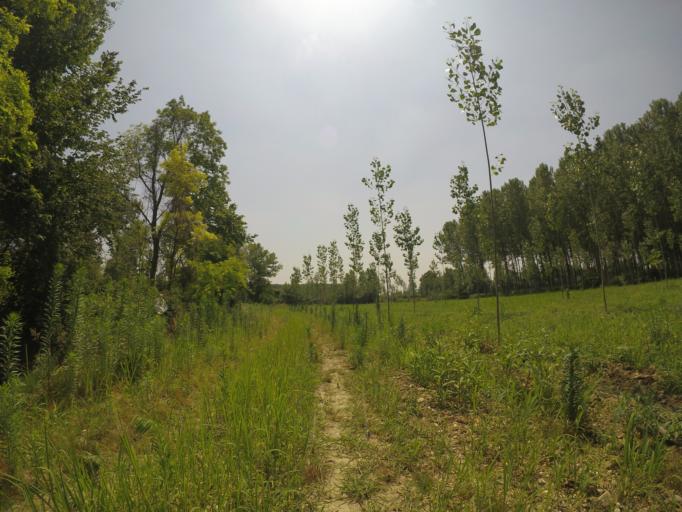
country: IT
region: Friuli Venezia Giulia
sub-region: Provincia di Udine
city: Bertiolo
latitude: 45.9296
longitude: 13.0533
